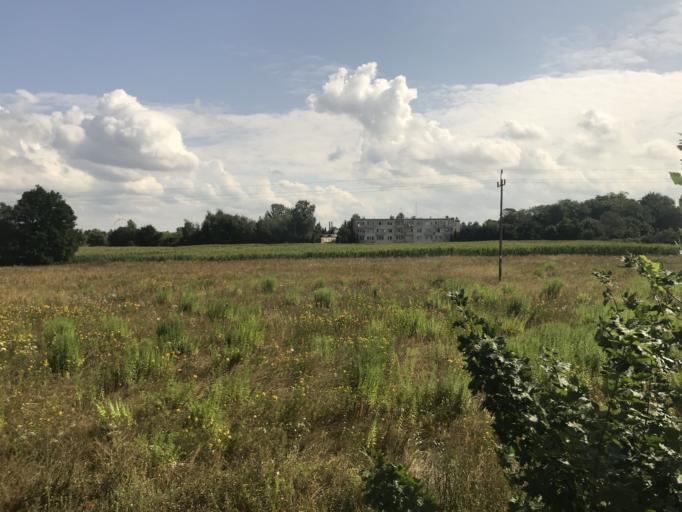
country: PL
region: Kujawsko-Pomorskie
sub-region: Powiat inowroclawski
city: Zlotniki Kujawskie
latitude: 52.9105
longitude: 18.1399
